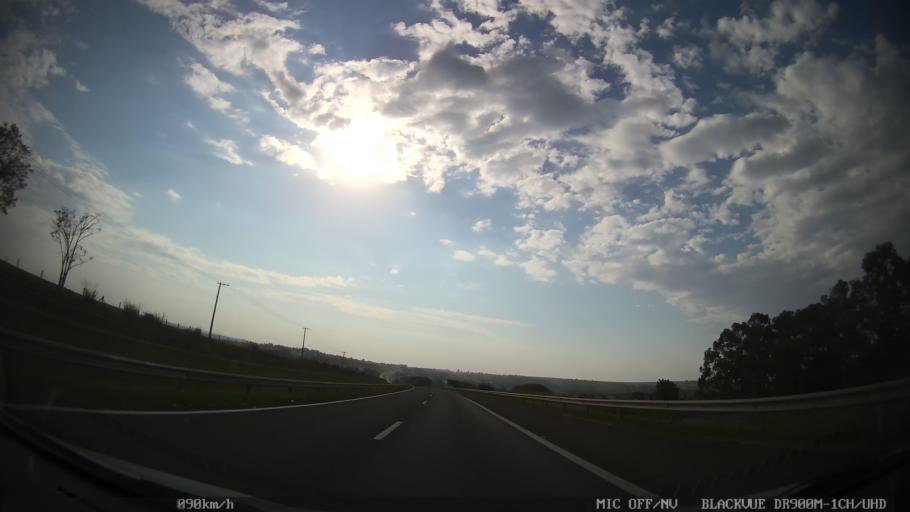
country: BR
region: Sao Paulo
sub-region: Paulinia
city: Paulinia
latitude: -22.7035
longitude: -47.1452
